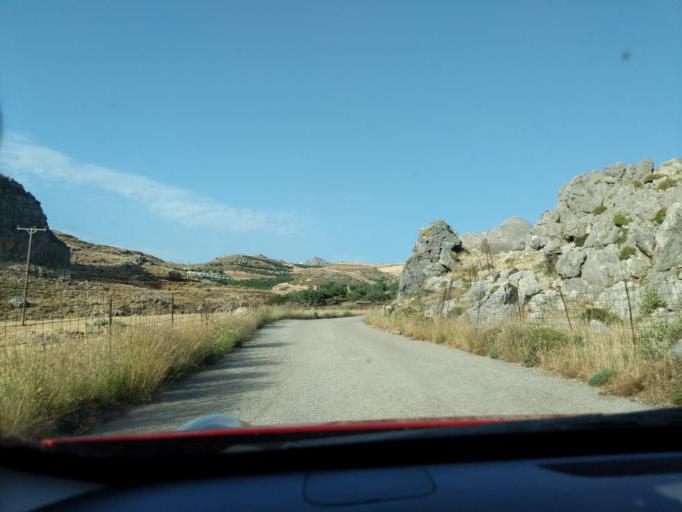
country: GR
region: Crete
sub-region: Nomos Rethymnis
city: Atsipopoulon
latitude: 35.1666
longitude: 24.4246
